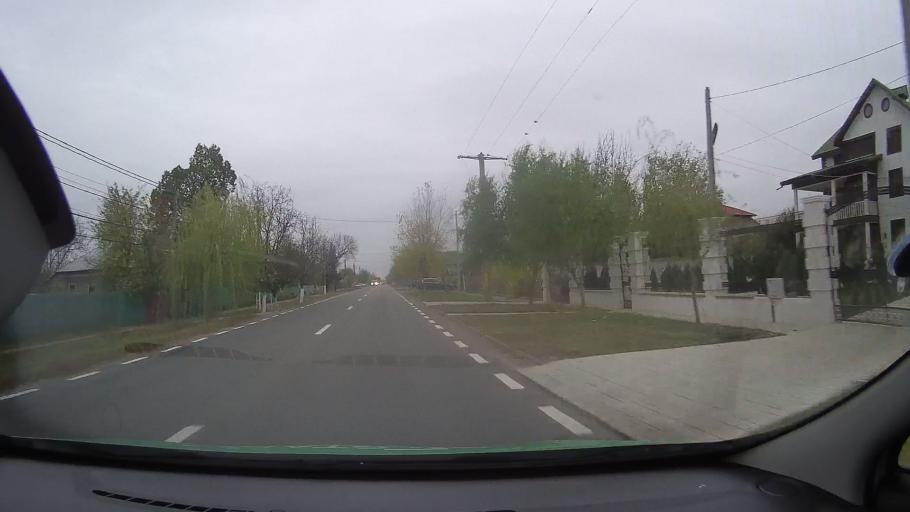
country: RO
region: Ialomita
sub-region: Comuna Slobozia
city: Slobozia
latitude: 44.6016
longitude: 27.3880
